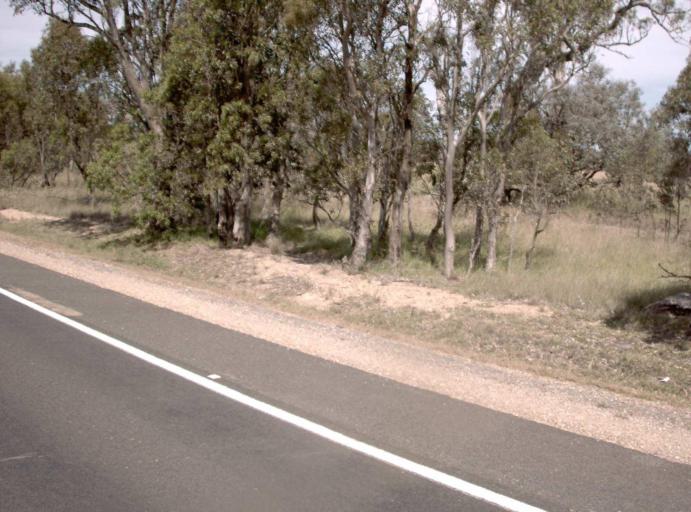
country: AU
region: Victoria
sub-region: East Gippsland
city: Bairnsdale
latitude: -37.8923
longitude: 147.3805
